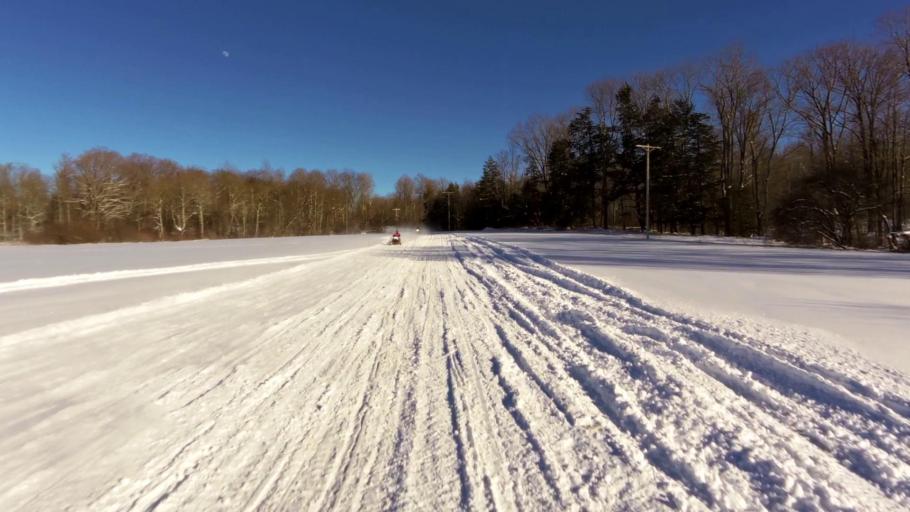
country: US
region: New York
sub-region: Chautauqua County
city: Mayville
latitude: 42.2756
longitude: -79.4637
